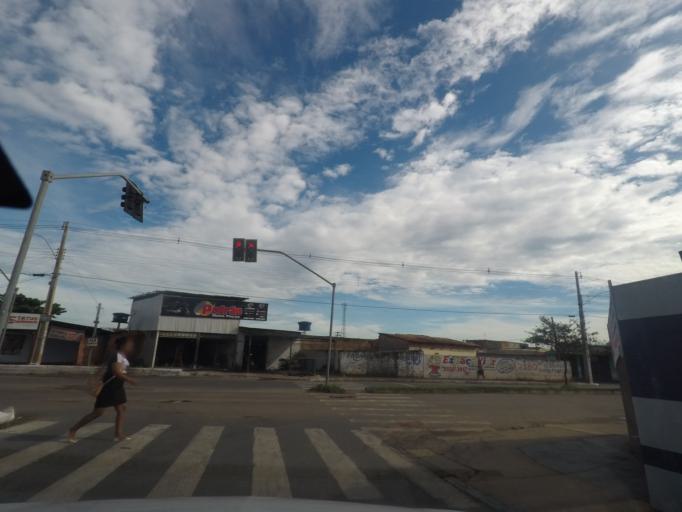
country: BR
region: Goias
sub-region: Aparecida De Goiania
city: Aparecida de Goiania
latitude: -16.8161
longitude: -49.3130
